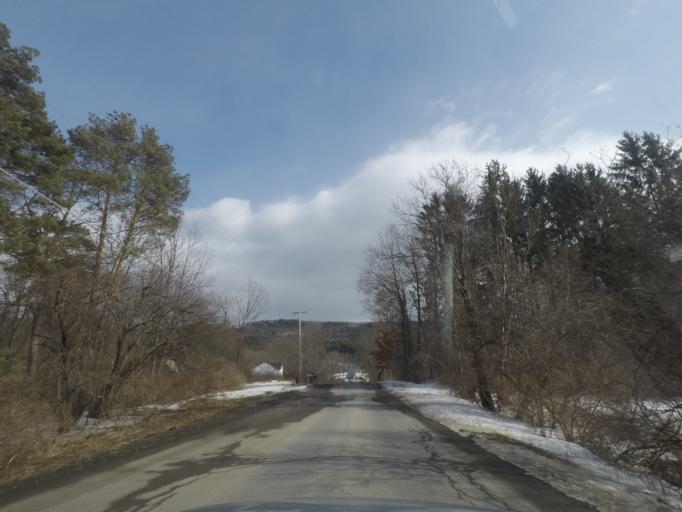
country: US
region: New York
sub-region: Rensselaer County
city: Poestenkill
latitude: 42.7724
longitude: -73.5473
